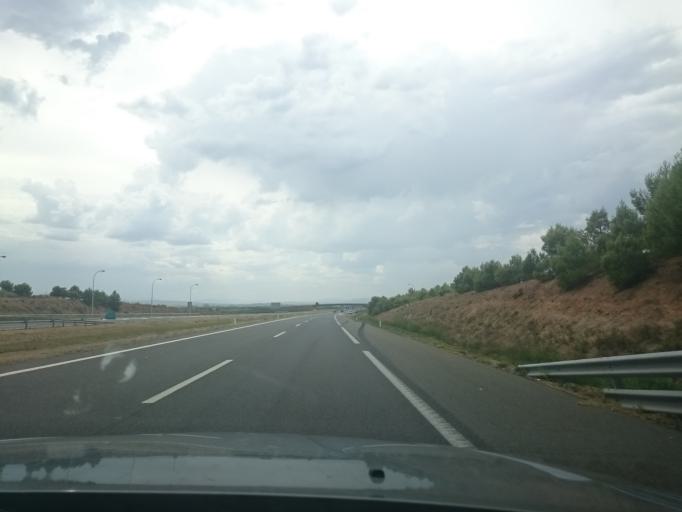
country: ES
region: Navarre
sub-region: Provincia de Navarra
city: Fontellas
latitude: 42.0141
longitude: -1.6031
